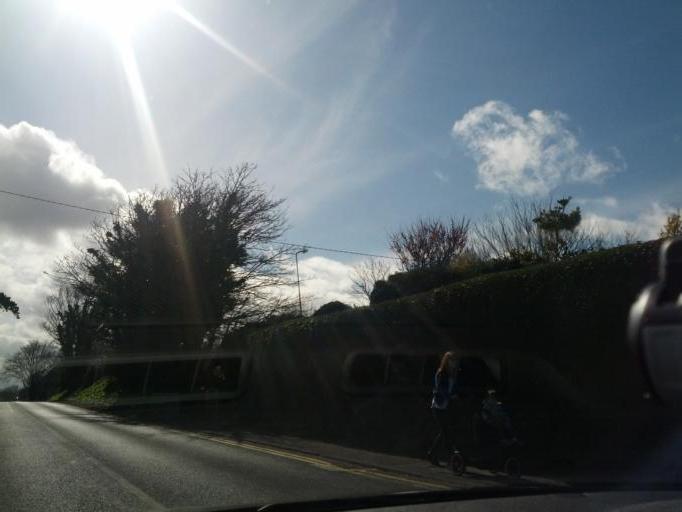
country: IE
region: Leinster
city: Portmarnock
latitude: 53.4302
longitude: -6.1267
